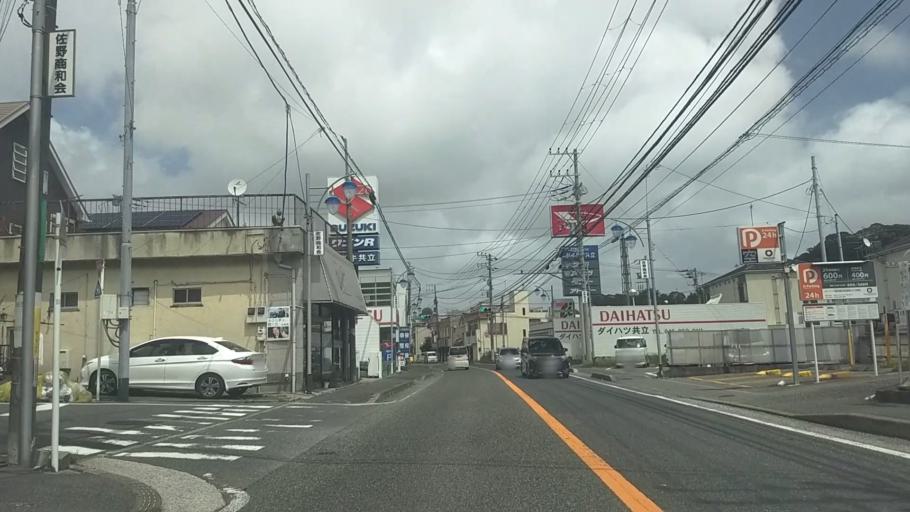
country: JP
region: Kanagawa
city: Yokosuka
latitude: 35.2624
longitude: 139.6689
